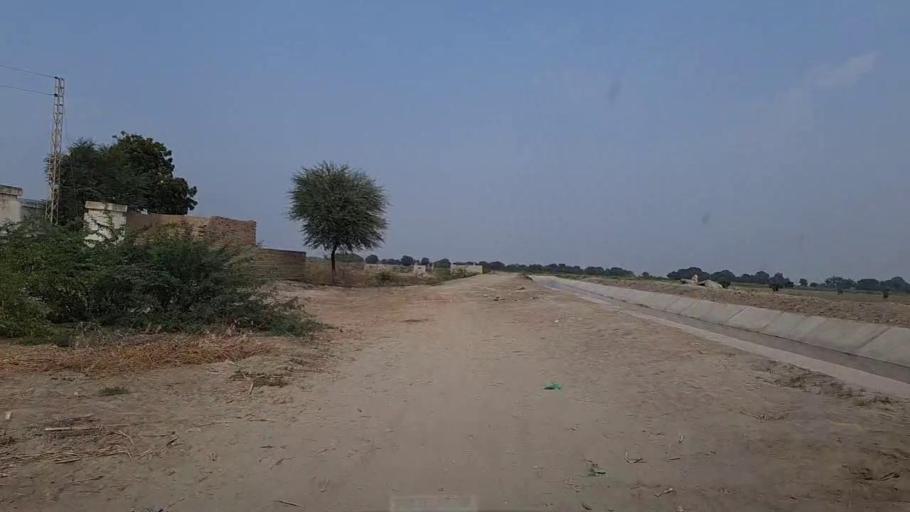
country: PK
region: Sindh
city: Mirwah Gorchani
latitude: 25.3890
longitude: 69.0621
